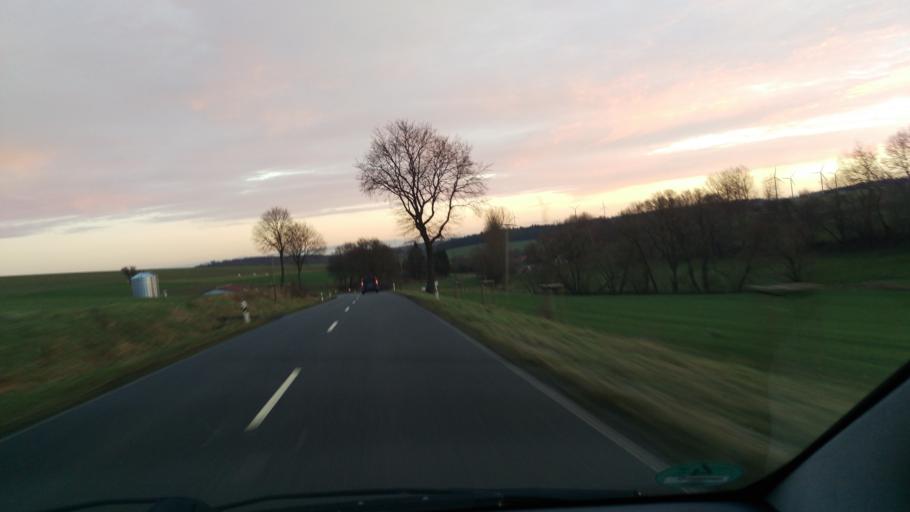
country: DE
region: Hesse
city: Kirtorf
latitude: 50.7539
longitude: 9.0563
